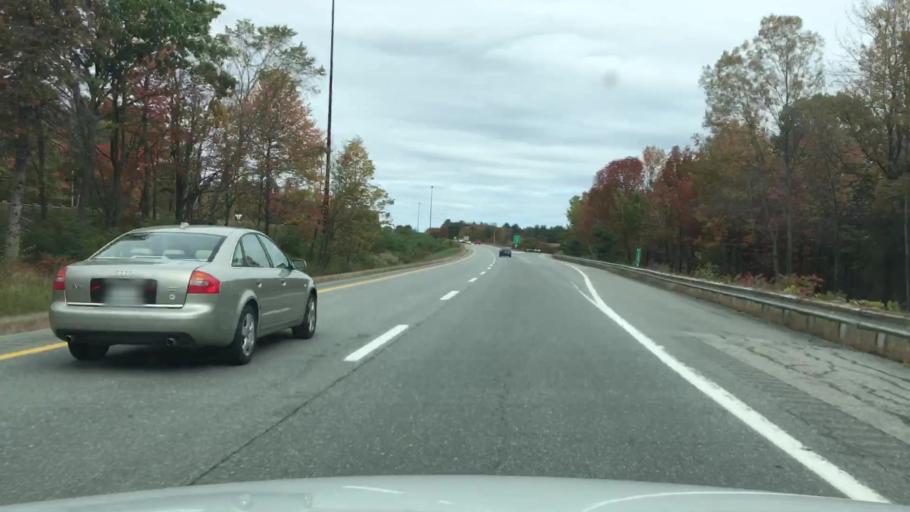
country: US
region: Maine
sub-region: Kennebec County
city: Oakland
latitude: 44.5415
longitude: -69.6818
